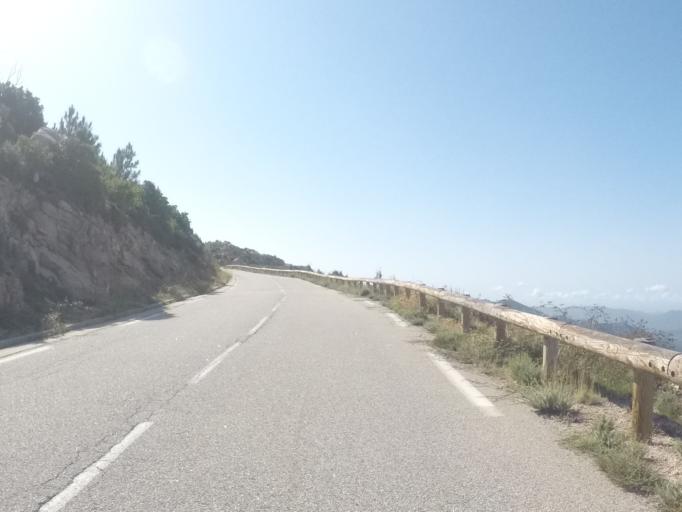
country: FR
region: Corsica
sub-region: Departement de la Corse-du-Sud
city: Olmeto
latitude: 41.7681
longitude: 9.0271
